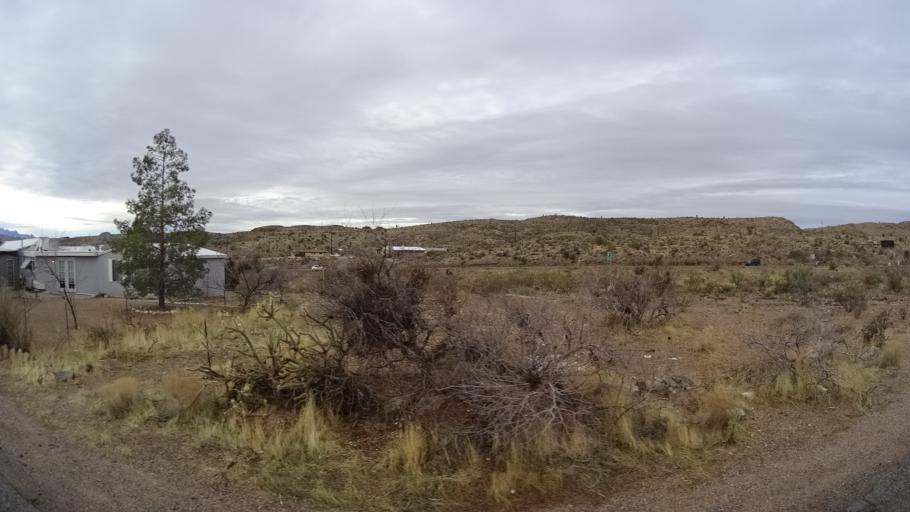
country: US
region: Arizona
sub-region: Mohave County
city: Kingman
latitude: 35.1992
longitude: -114.0767
